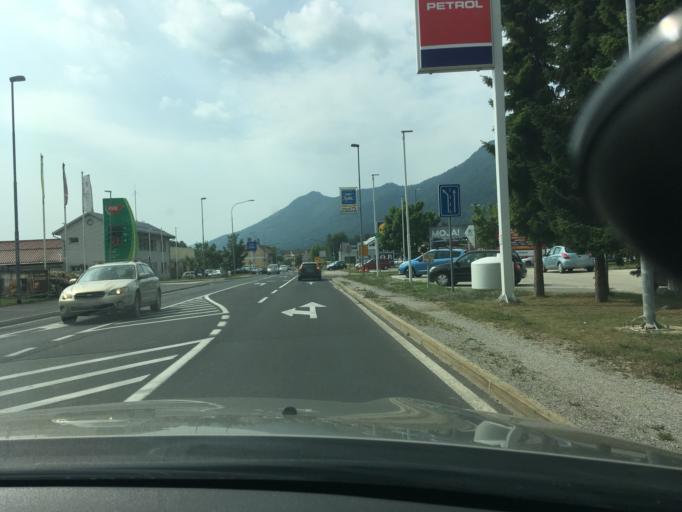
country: SI
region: Kocevje
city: Kocevje
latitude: 45.6489
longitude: 14.8539
